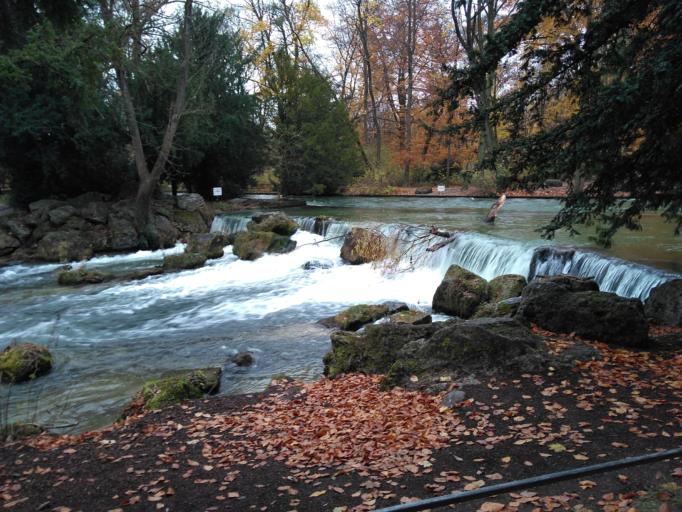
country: DE
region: Bavaria
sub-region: Upper Bavaria
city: Munich
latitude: 48.1460
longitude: 11.5866
